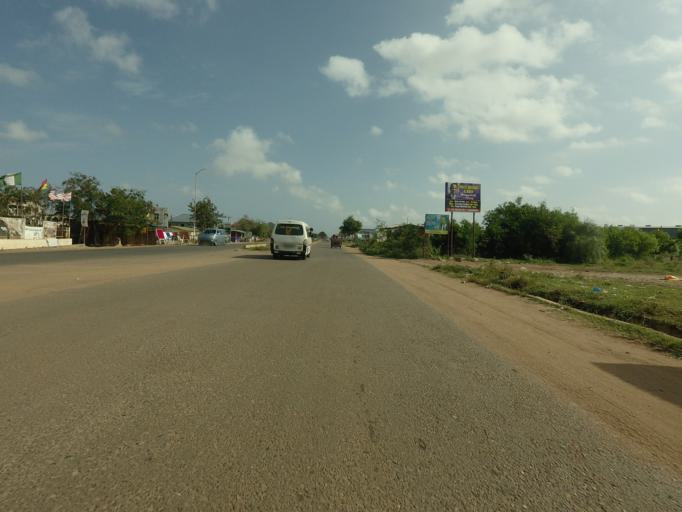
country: GH
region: Greater Accra
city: Tema
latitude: 5.6711
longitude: -0.0463
